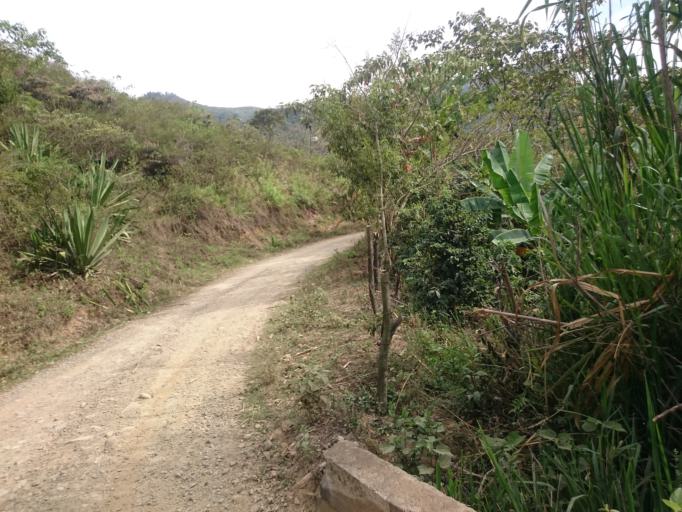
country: CO
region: Cauca
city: Suarez
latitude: 2.9316
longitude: -76.7185
